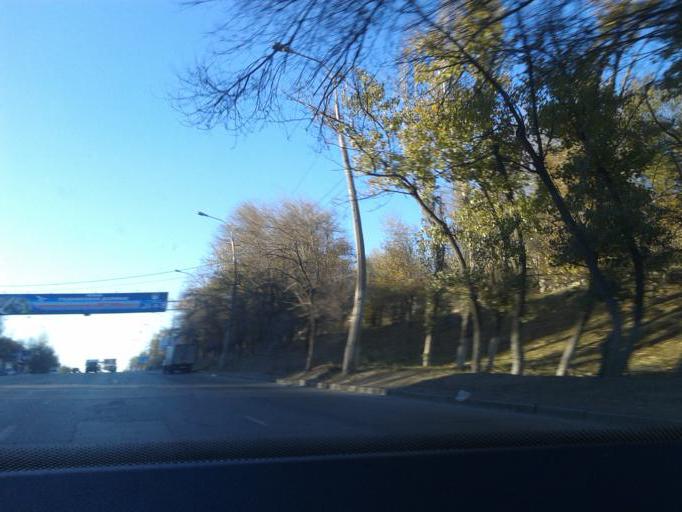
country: RU
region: Volgograd
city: Volgograd
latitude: 48.6787
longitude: 44.4451
